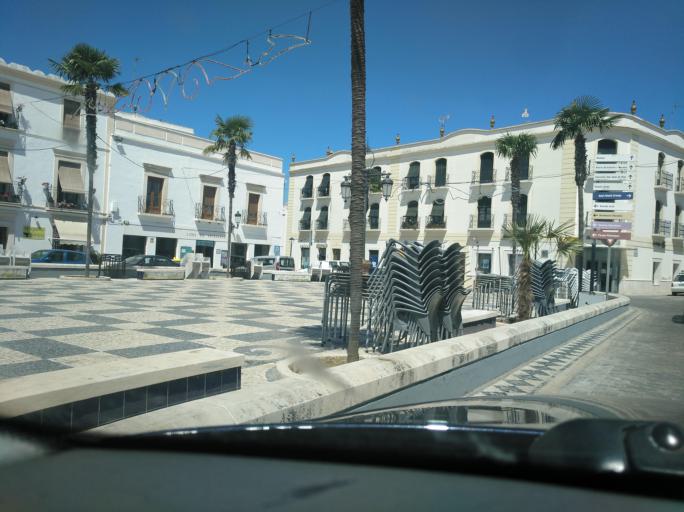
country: ES
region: Extremadura
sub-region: Provincia de Badajoz
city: Olivenza
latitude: 38.6845
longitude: -7.1022
